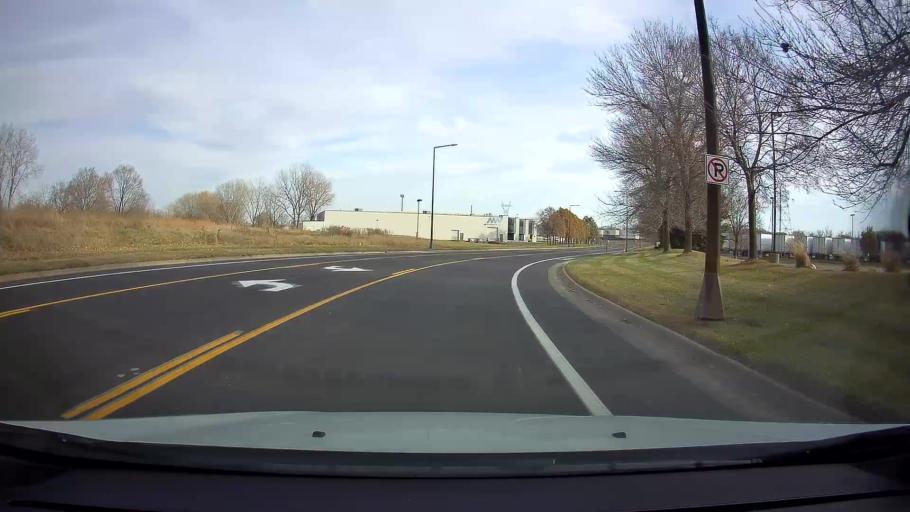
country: US
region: Minnesota
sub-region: Ramsey County
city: Falcon Heights
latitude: 44.9731
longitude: -93.1796
